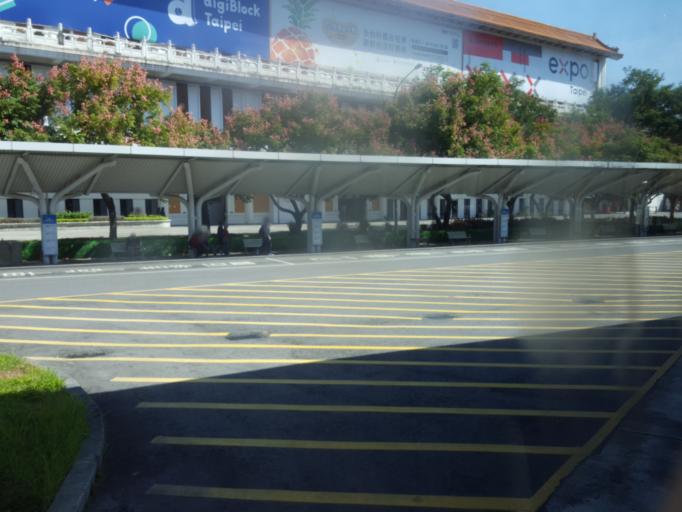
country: TW
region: Taipei
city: Taipei
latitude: 25.0699
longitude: 121.5200
